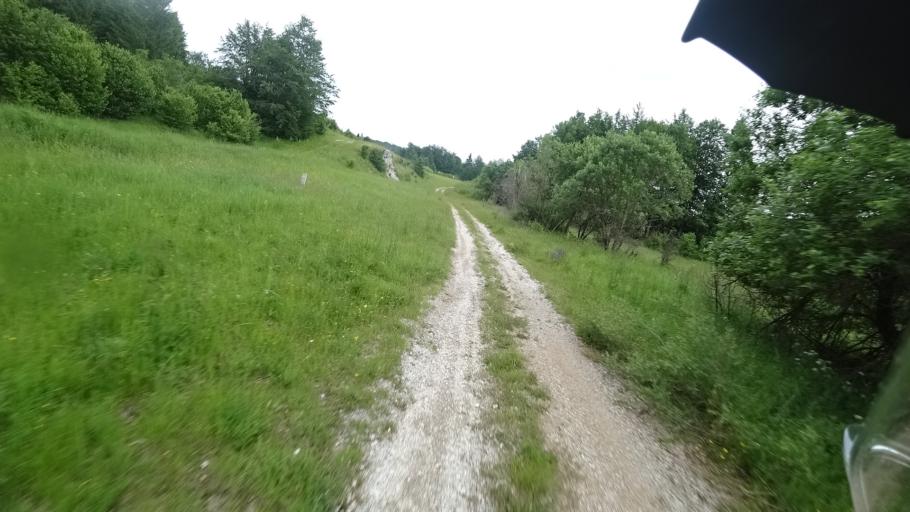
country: HR
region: Primorsko-Goranska
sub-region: Grad Delnice
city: Delnice
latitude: 45.3882
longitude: 14.8374
